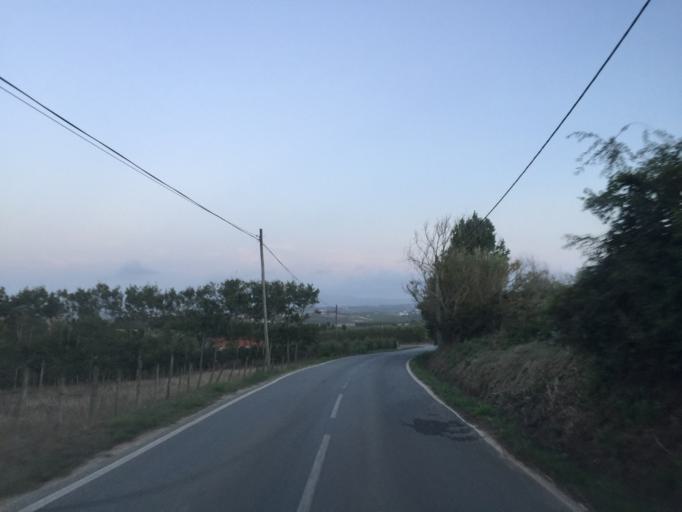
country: PT
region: Leiria
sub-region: Bombarral
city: Bombarral
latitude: 39.2765
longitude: -9.1854
